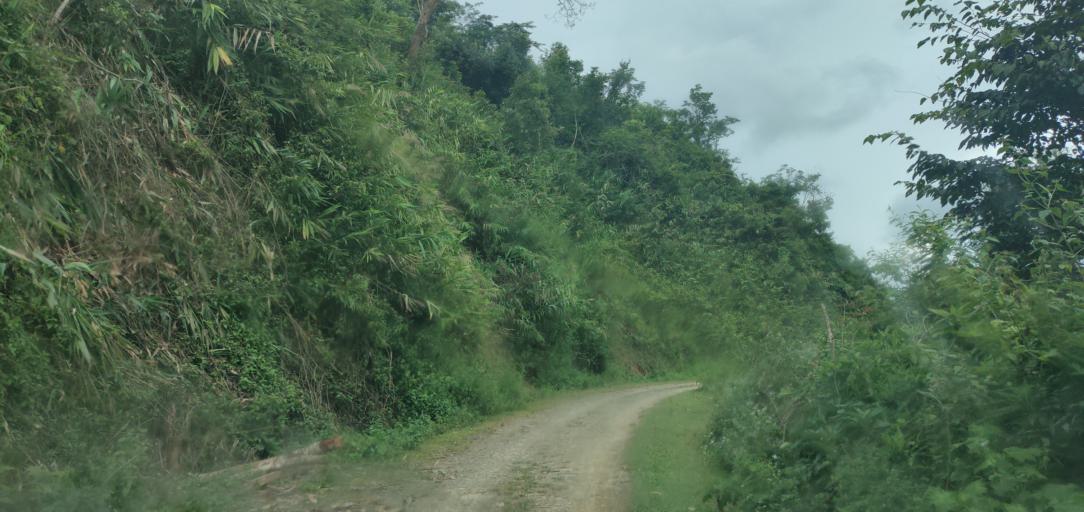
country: LA
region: Phongsali
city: Phongsali
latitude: 21.4476
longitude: 102.3087
